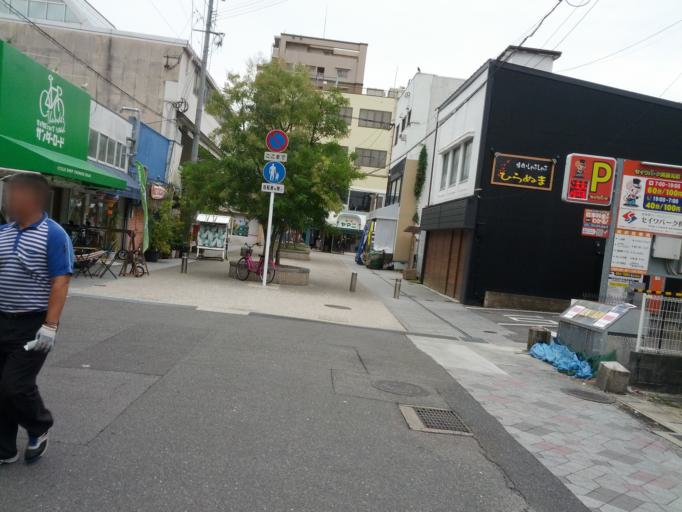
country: JP
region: Saga Prefecture
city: Saga-shi
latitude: 33.2537
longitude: 130.3033
